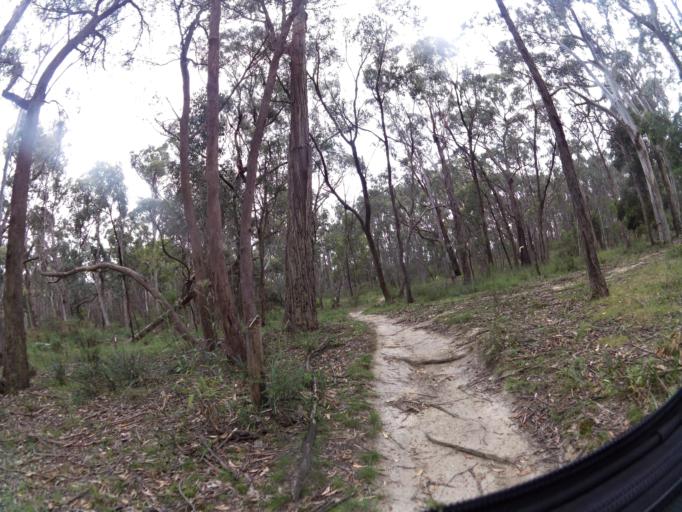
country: AU
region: Victoria
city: Brown Hill
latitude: -37.4600
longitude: 143.9076
